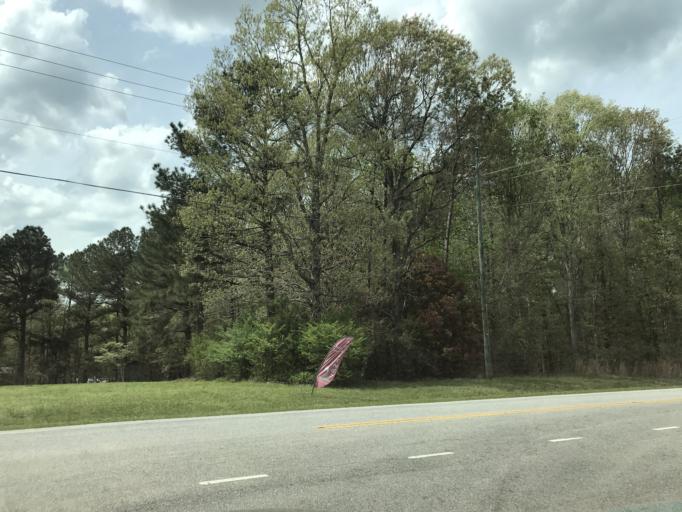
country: US
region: North Carolina
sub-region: Nash County
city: Spring Hope
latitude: 35.9645
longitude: -78.2083
